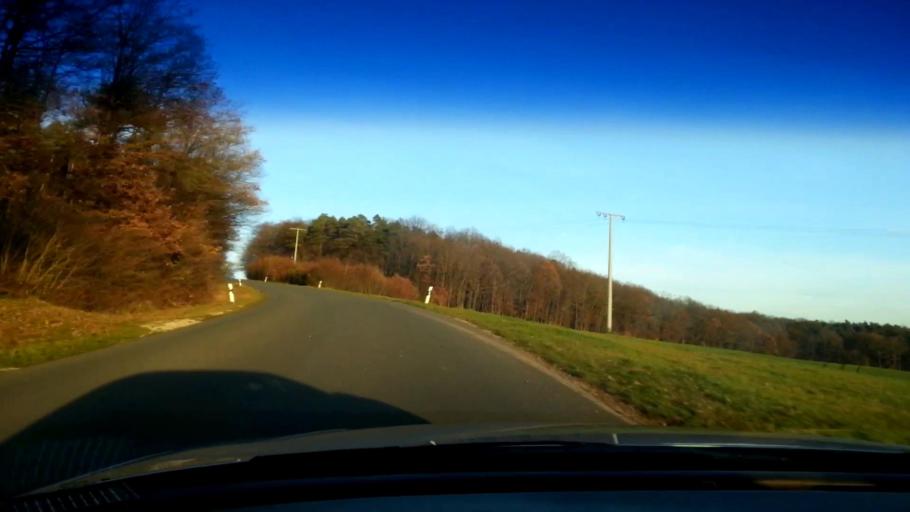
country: DE
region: Bavaria
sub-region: Upper Franconia
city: Rattelsdorf
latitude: 50.0587
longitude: 10.8913
